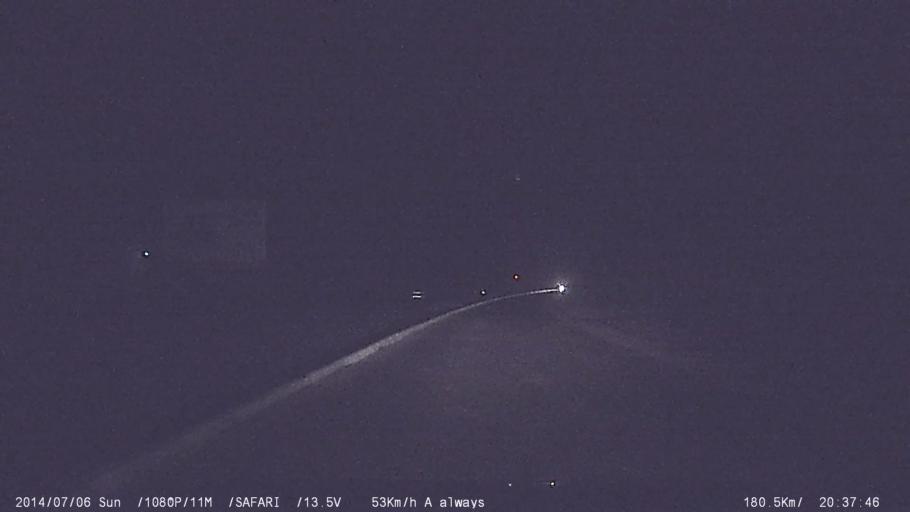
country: IN
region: Kerala
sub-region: Palakkad district
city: Chittur
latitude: 10.8241
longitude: 76.8151
